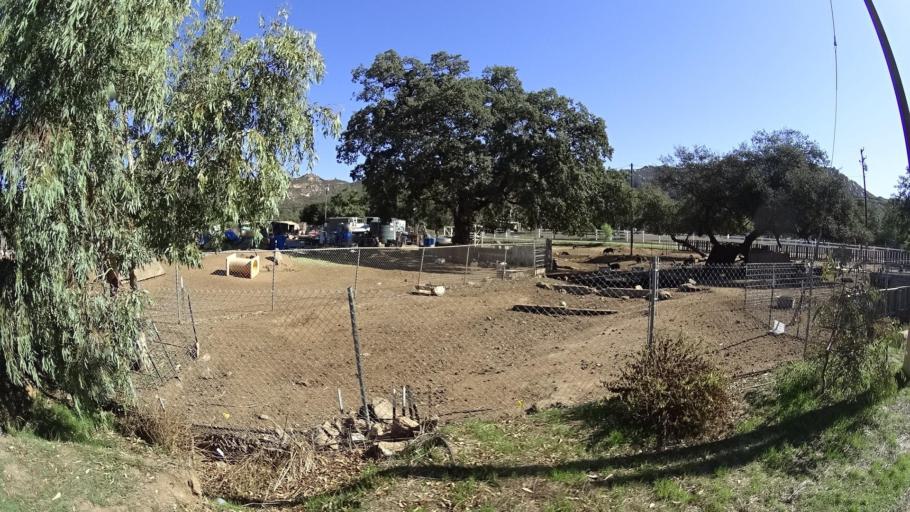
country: US
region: California
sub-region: San Diego County
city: Jamul
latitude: 32.7236
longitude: -116.8127
